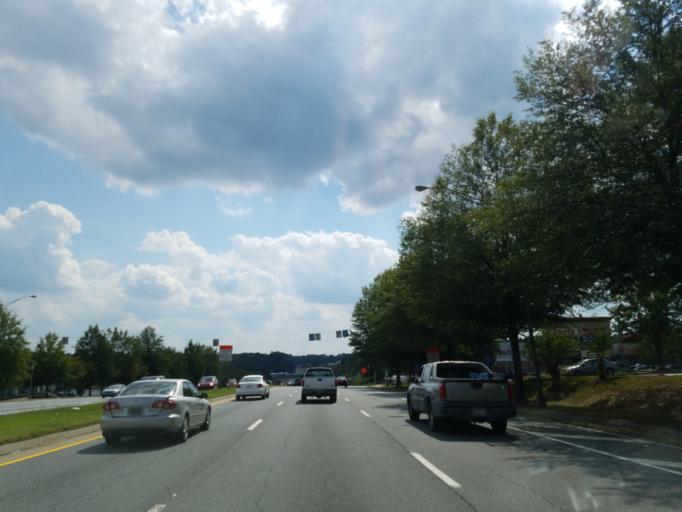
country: US
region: Georgia
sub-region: Gwinnett County
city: Buford
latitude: 34.0610
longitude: -83.9917
